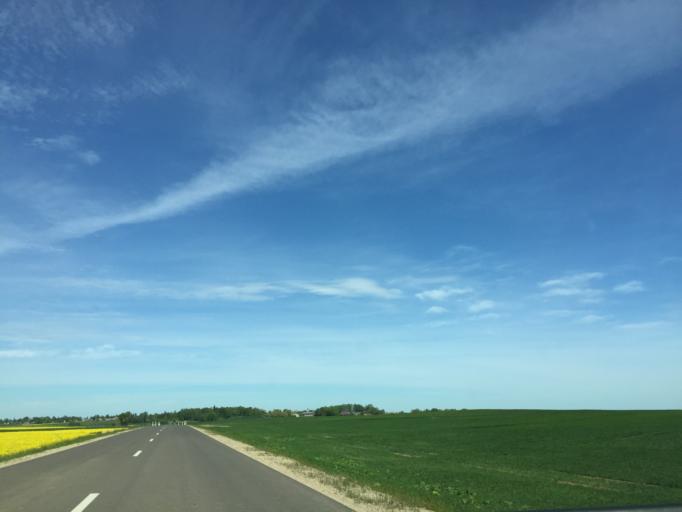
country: LT
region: Panevezys
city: Pasvalys
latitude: 56.1091
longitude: 24.2472
